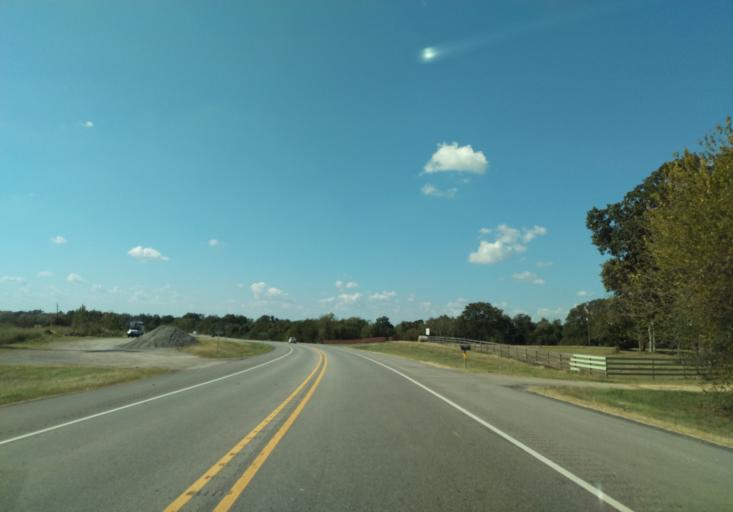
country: US
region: Texas
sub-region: Montgomery County
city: Magnolia
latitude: 30.3912
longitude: -95.7347
